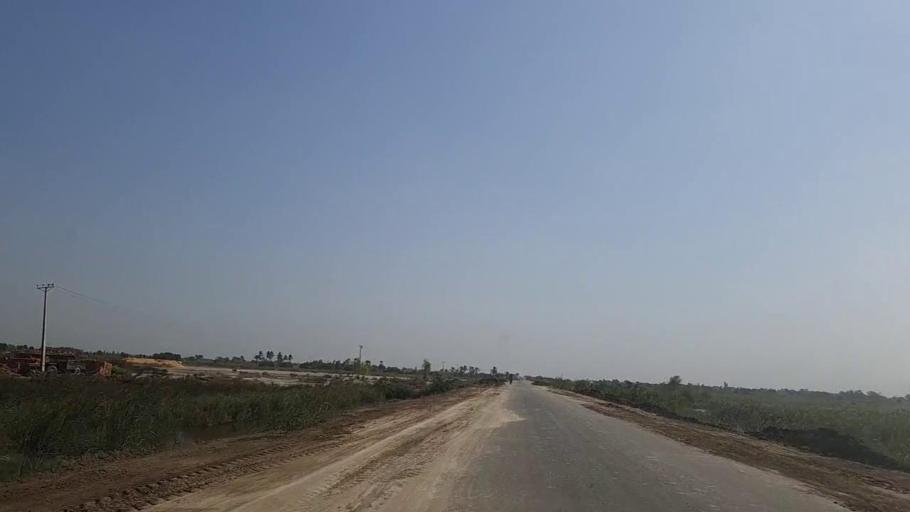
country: PK
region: Sindh
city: Daro Mehar
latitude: 24.7854
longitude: 68.1930
